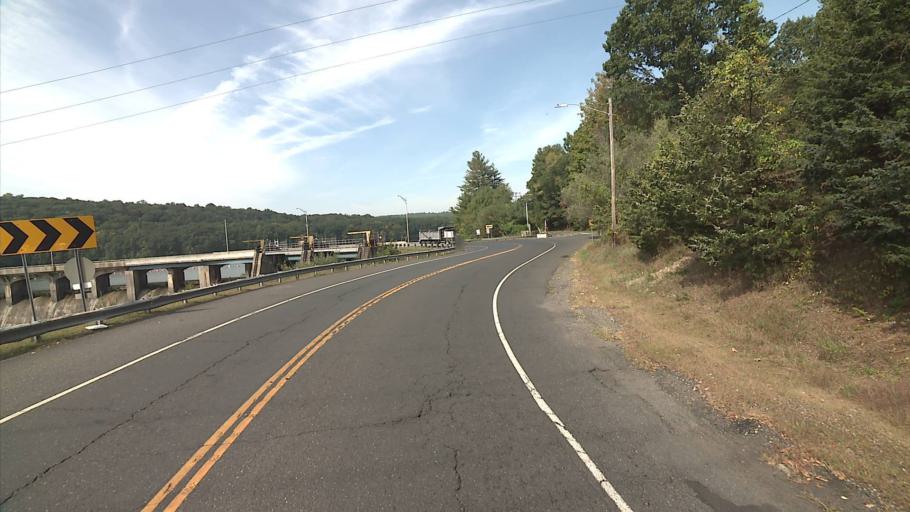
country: US
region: Connecticut
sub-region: New Haven County
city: Oxford
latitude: 41.3844
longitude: -73.1701
